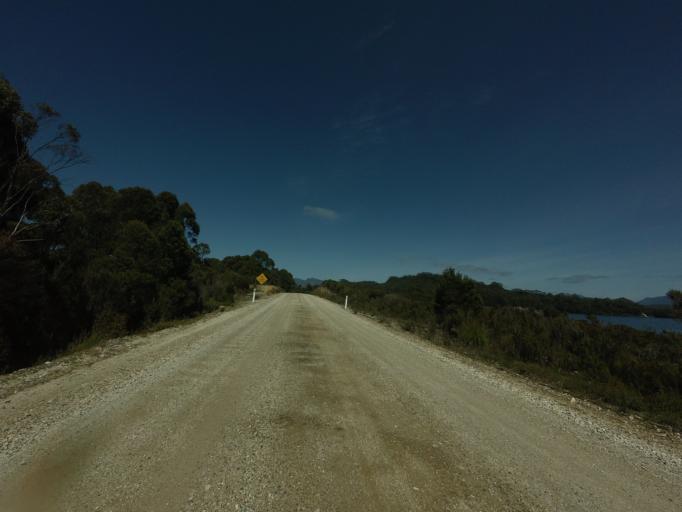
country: AU
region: Tasmania
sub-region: Huon Valley
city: Geeveston
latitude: -43.0275
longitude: 146.3525
